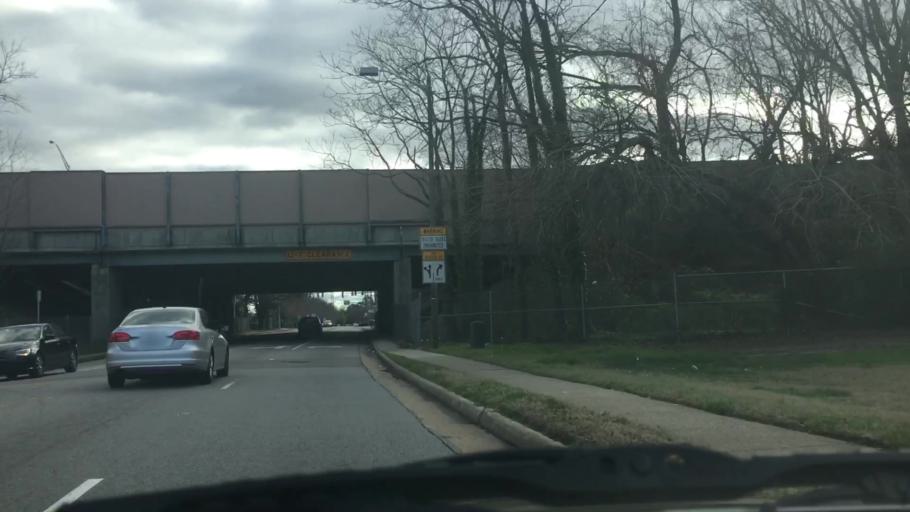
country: US
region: Virginia
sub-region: City of Norfolk
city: Norfolk
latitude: 36.9040
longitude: -76.2429
